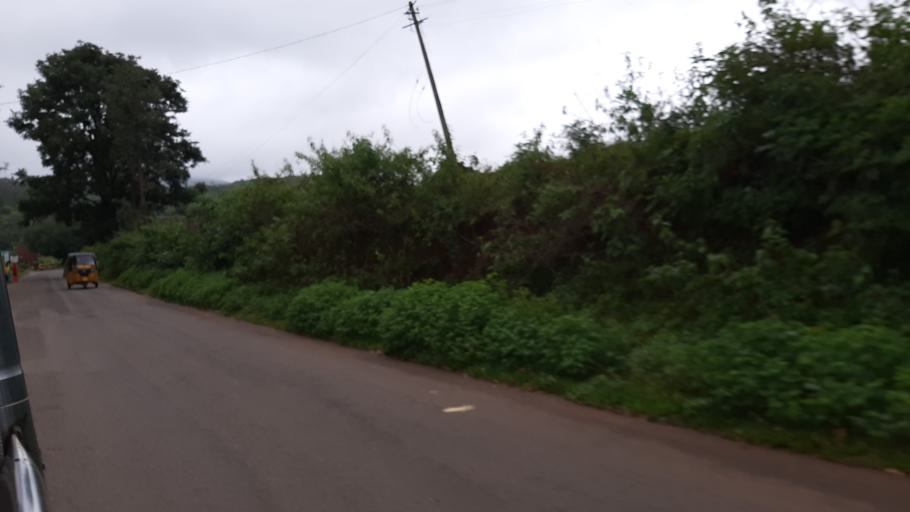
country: IN
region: Andhra Pradesh
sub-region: Vizianagaram District
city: Salur
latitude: 18.2864
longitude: 82.9387
